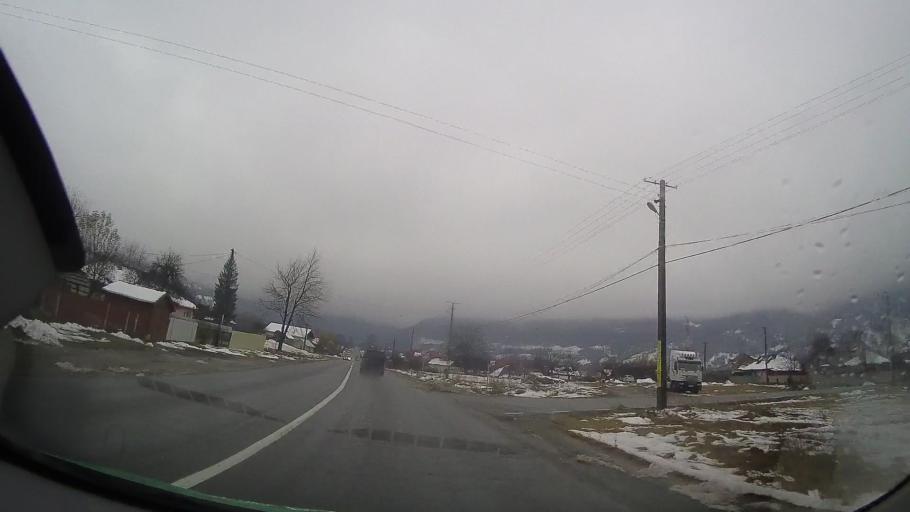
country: RO
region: Neamt
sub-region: Comuna Pangarati
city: Stejaru
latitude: 46.9104
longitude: 26.1790
